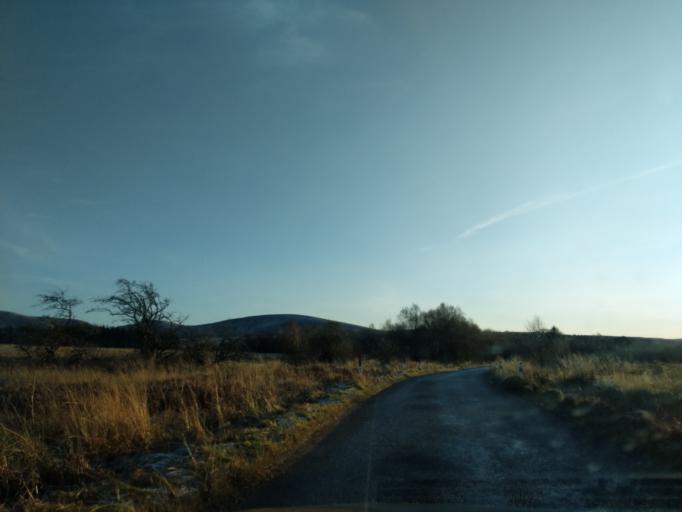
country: GB
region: Scotland
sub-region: Edinburgh
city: Balerno
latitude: 55.8630
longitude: -3.3329
